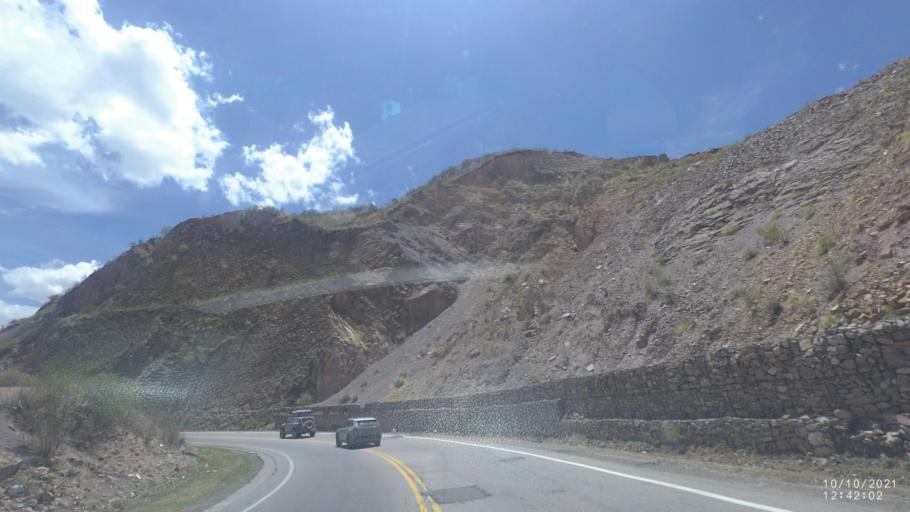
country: BO
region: Cochabamba
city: Irpa Irpa
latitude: -17.6308
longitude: -66.3898
